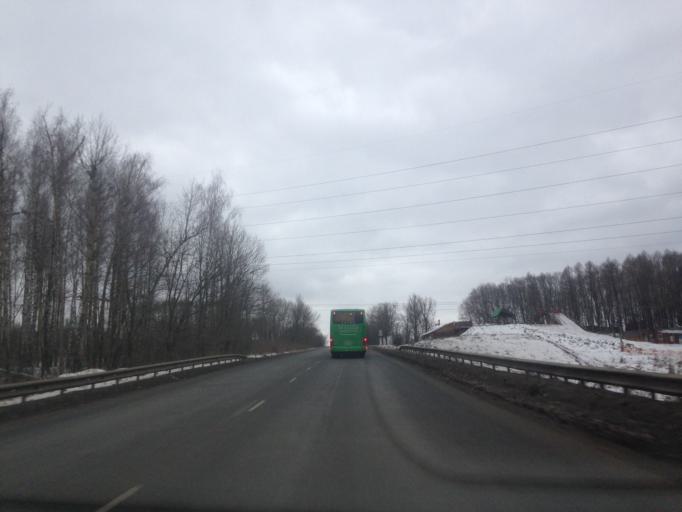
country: RU
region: Tula
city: Mendeleyevskiy
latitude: 54.1241
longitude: 37.5733
